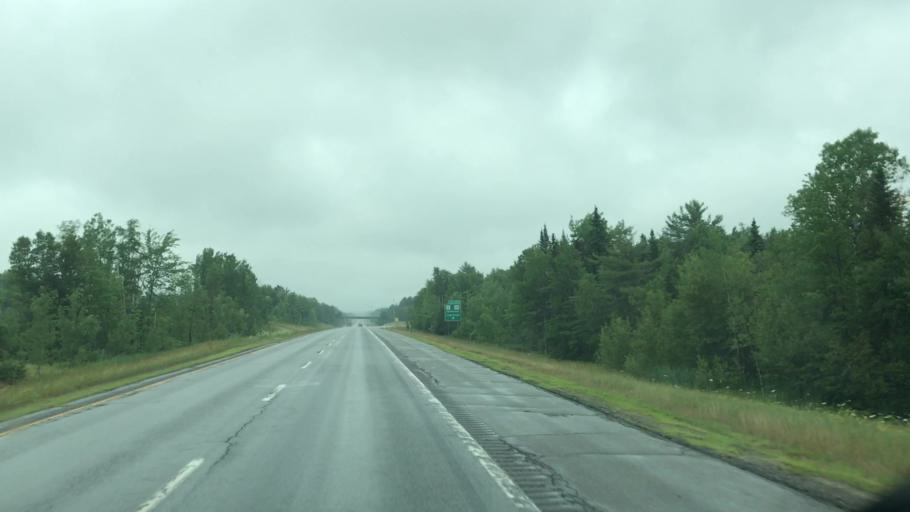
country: US
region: Maine
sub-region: Penobscot County
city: Howland
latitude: 45.2296
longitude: -68.6759
